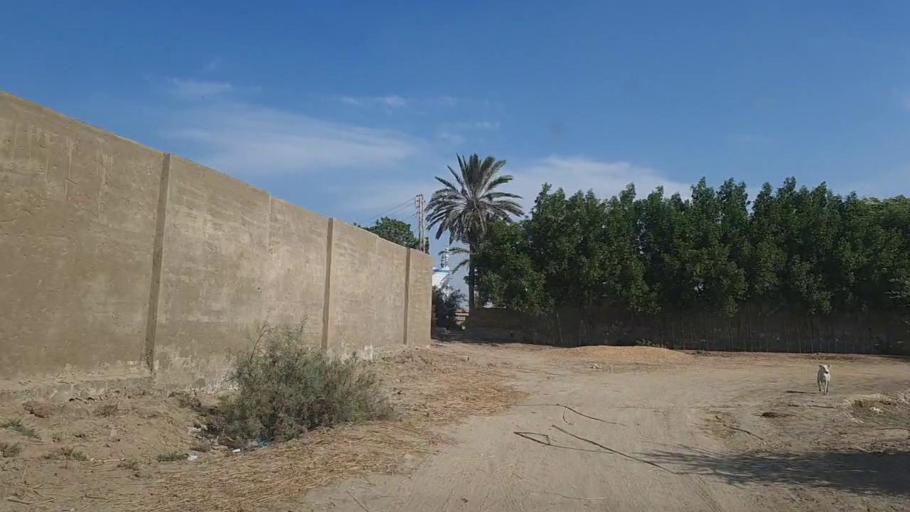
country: PK
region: Sindh
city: Bulri
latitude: 24.8737
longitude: 68.2751
